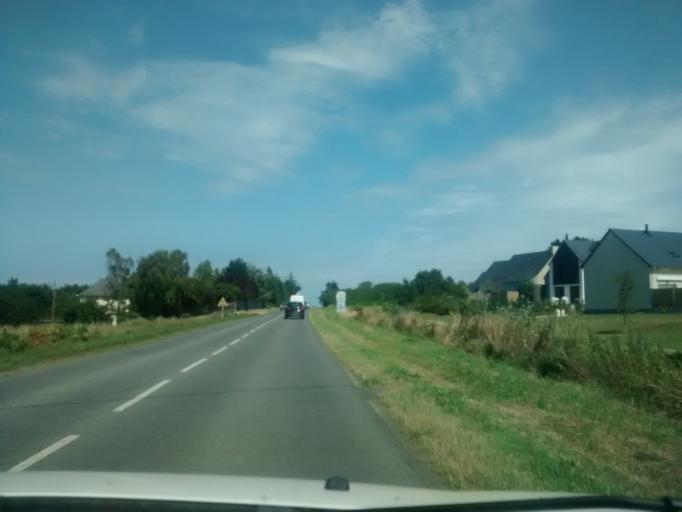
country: FR
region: Brittany
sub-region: Departement d'Ille-et-Vilaine
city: Cancale
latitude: 48.6867
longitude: -1.8529
